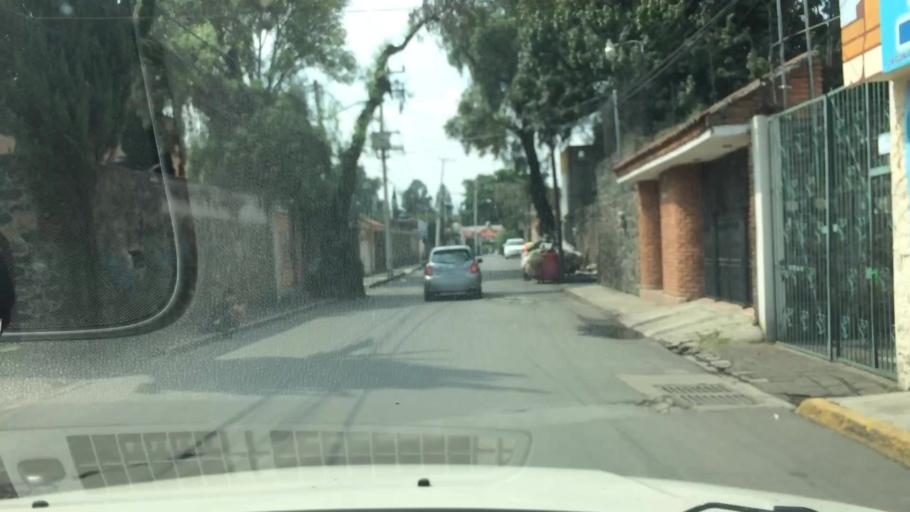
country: MX
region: Mexico City
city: Tlalpan
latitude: 19.2697
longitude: -99.1443
